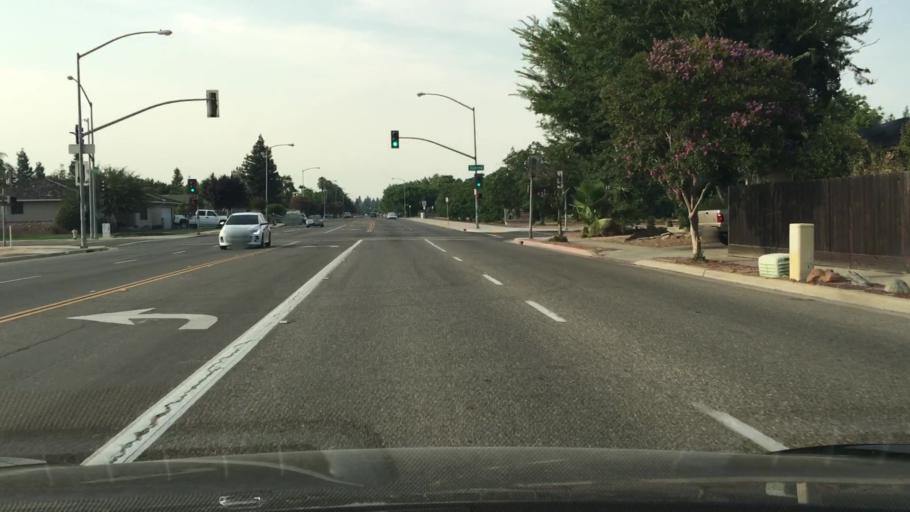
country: US
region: California
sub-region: Fresno County
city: Clovis
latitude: 36.8299
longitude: -119.7361
